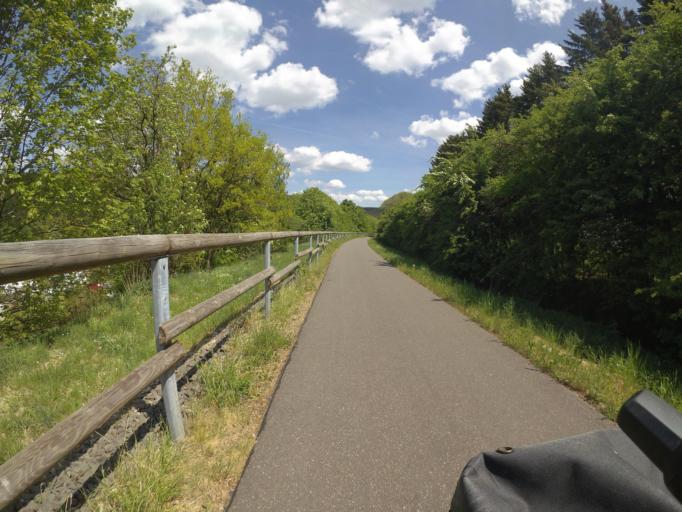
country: DE
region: Rheinland-Pfalz
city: Hallschlag
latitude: 50.3611
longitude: 6.4533
